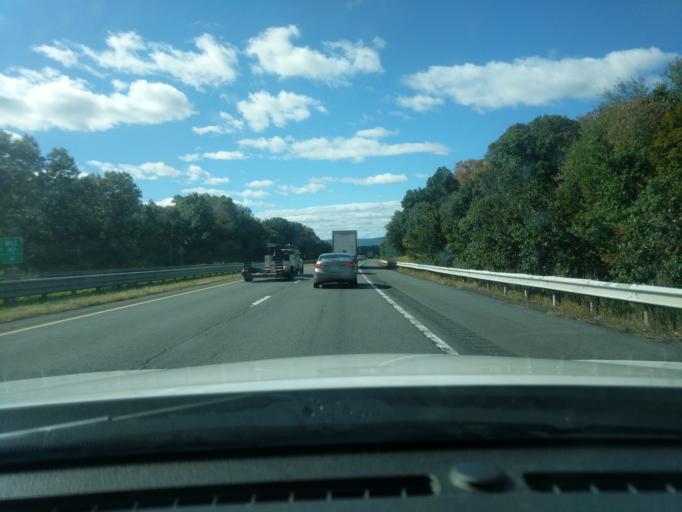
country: US
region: Massachusetts
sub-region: Hampden County
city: Westfield
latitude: 42.1391
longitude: -72.6940
